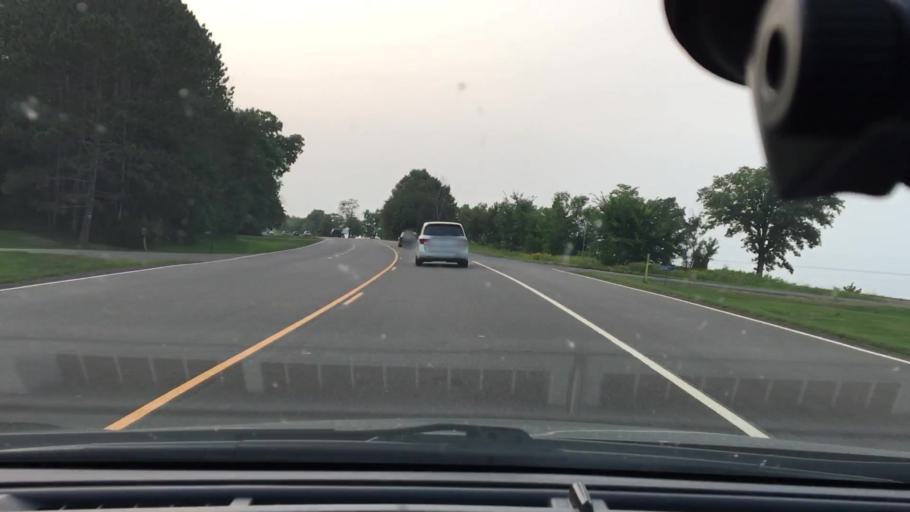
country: US
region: Minnesota
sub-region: Mille Lacs County
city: Vineland
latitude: 46.1341
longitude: -93.6914
